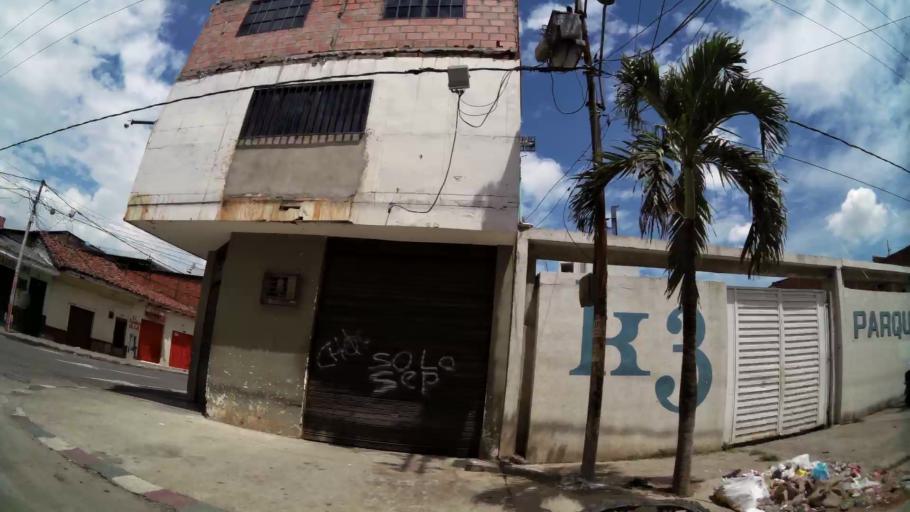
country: CO
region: Valle del Cauca
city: Cali
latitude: 3.4452
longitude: -76.5216
